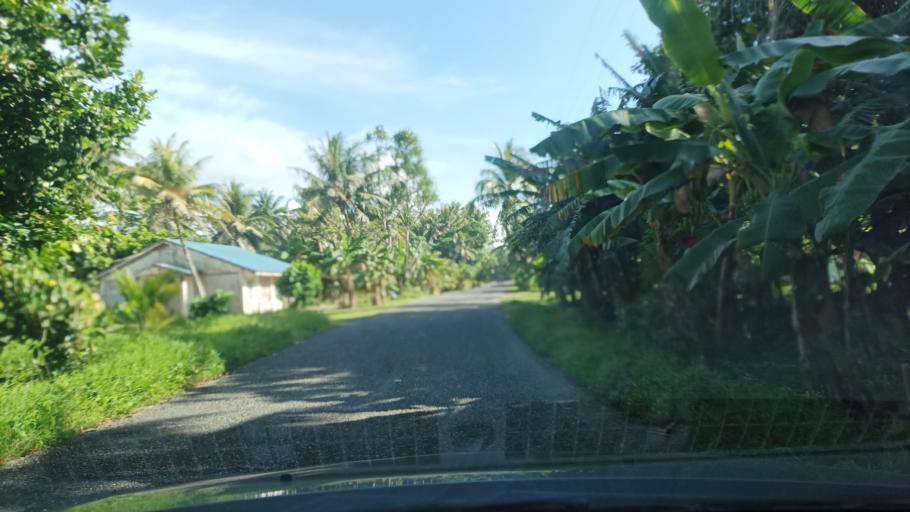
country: FM
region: Kosrae
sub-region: Malem Municipality
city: Malem
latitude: 5.2942
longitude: 163.0297
